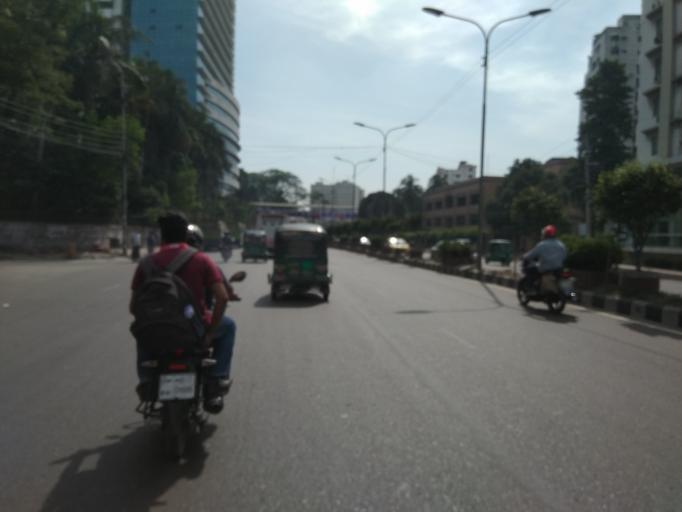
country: BD
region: Dhaka
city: Azimpur
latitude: 23.7443
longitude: 90.3953
